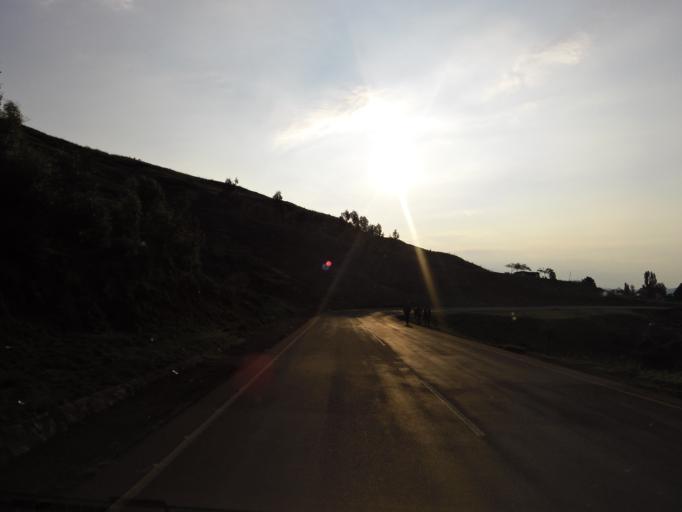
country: LS
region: Butha-Buthe
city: Butha-Buthe
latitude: -29.0360
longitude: 28.2886
